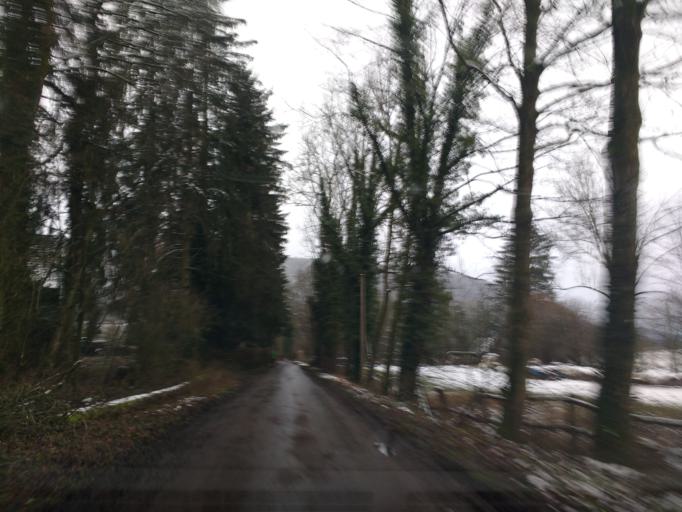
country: DE
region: North Rhine-Westphalia
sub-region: Regierungsbezirk Detmold
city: Altenbeken
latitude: 51.7612
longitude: 8.9072
